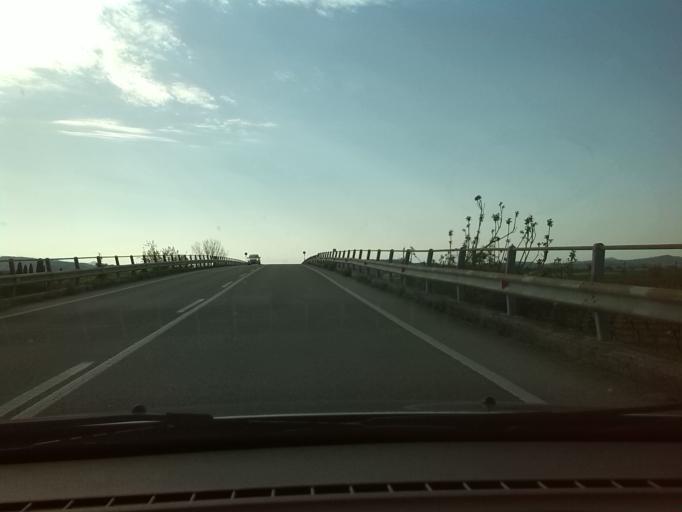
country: IT
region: Friuli Venezia Giulia
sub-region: Provincia di Udine
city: Cividale del Friuli
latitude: 46.0698
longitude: 13.4271
